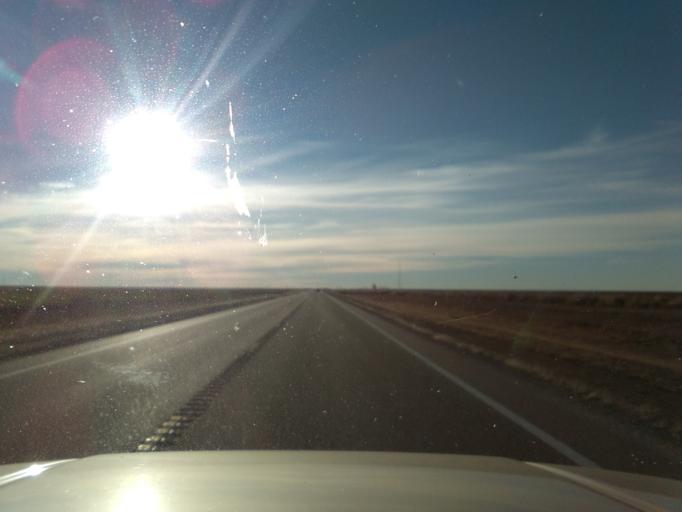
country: US
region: Kansas
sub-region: Sheridan County
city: Hoxie
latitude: 39.4874
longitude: -100.6986
